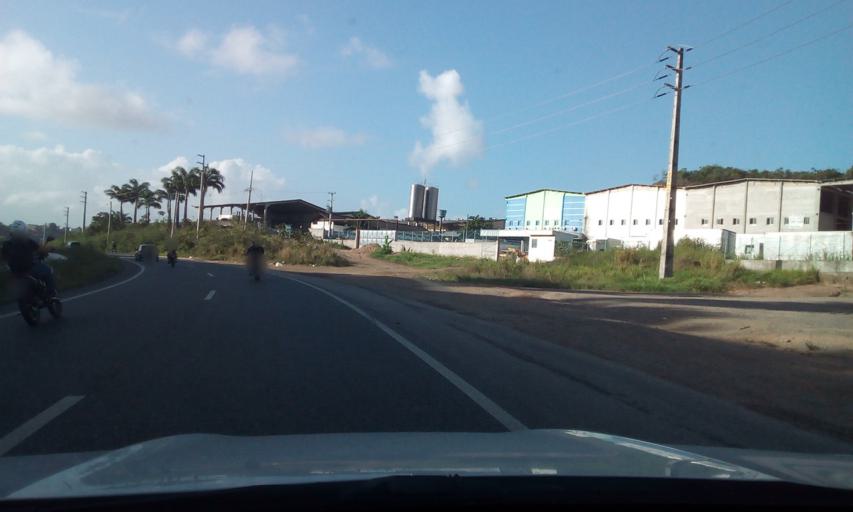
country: BR
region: Pernambuco
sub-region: Paulista
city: Paulista
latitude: -7.9820
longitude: -34.9321
